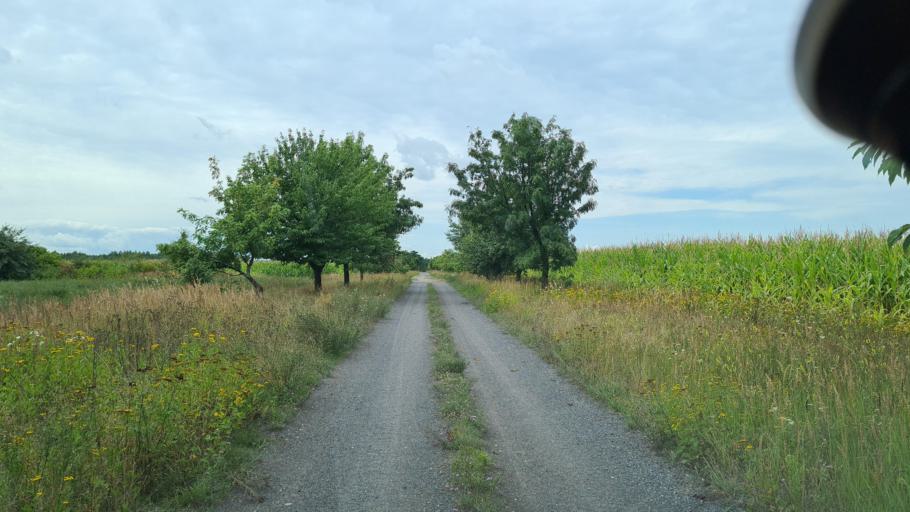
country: DE
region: Brandenburg
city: Spremberg
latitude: 51.5735
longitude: 14.2969
